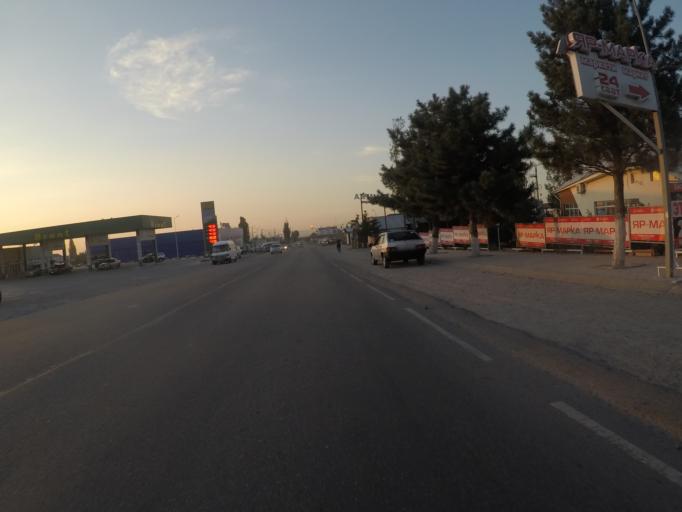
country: KG
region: Chuy
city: Lebedinovka
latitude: 42.8017
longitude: 74.6490
